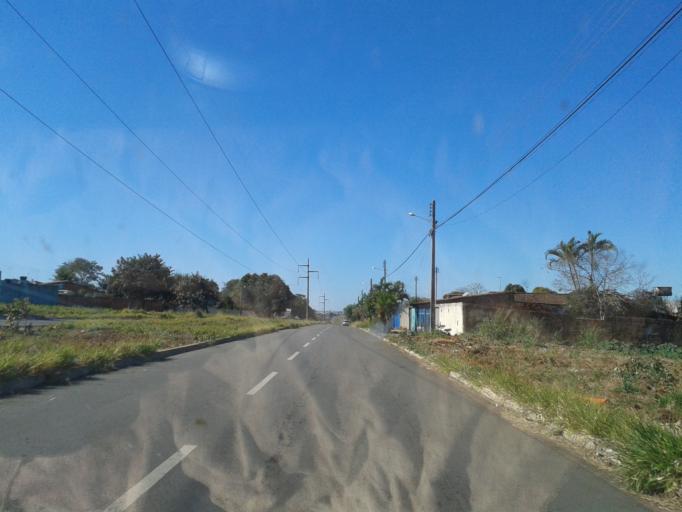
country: BR
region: Goias
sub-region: Aparecida De Goiania
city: Aparecida de Goiania
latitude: -16.7604
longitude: -49.3087
